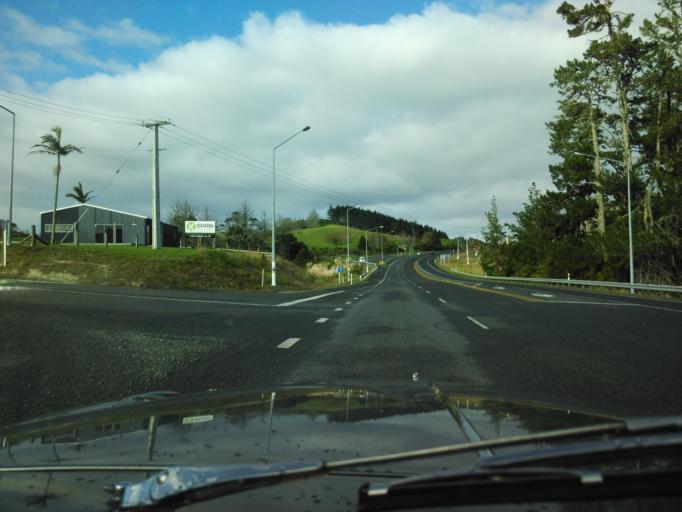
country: NZ
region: Auckland
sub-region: Auckland
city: Wellsford
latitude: -36.2358
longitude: 174.5111
